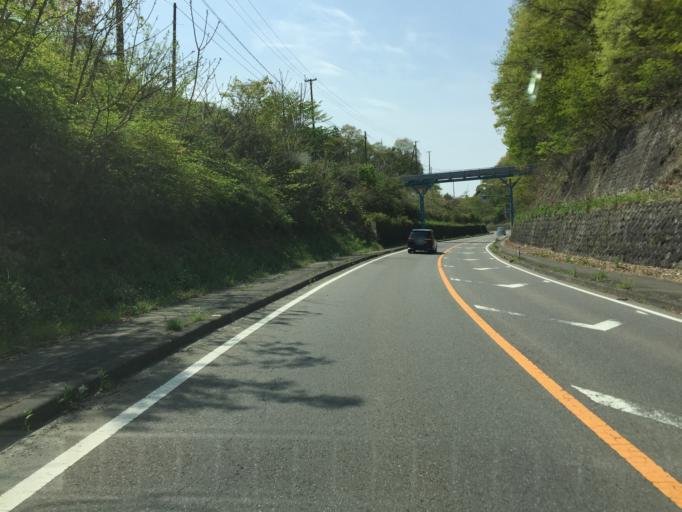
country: JP
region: Fukushima
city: Nihommatsu
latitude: 37.6452
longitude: 140.4639
